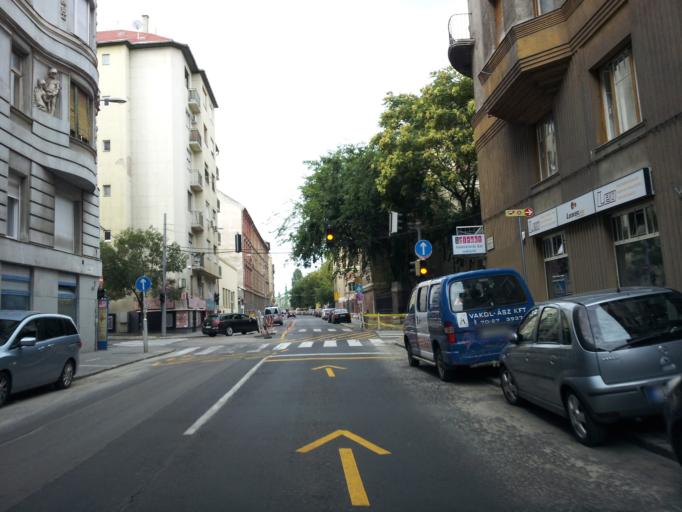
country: HU
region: Budapest
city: Budapest IX. keruelet
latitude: 47.4792
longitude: 19.0538
